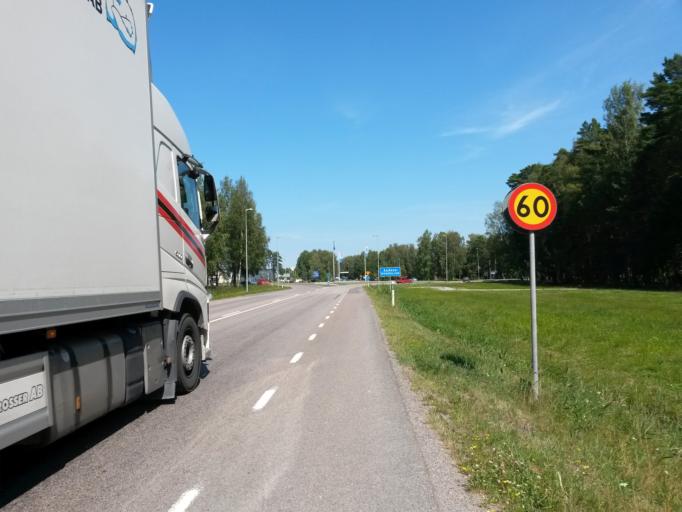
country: SE
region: Vaestra Goetaland
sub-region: Lidkopings Kommun
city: Lidkoping
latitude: 58.4914
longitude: 13.1413
